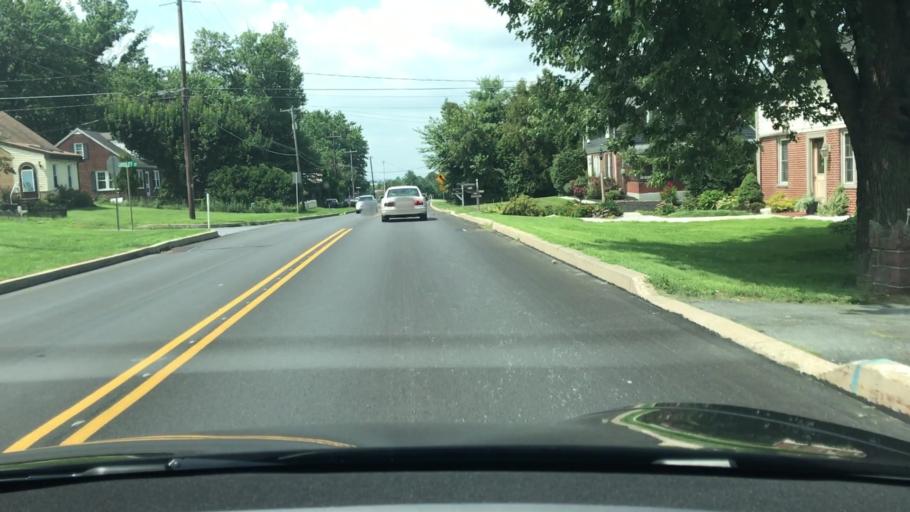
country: US
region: Pennsylvania
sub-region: Lancaster County
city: Mountville
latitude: 40.0608
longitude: -76.4065
